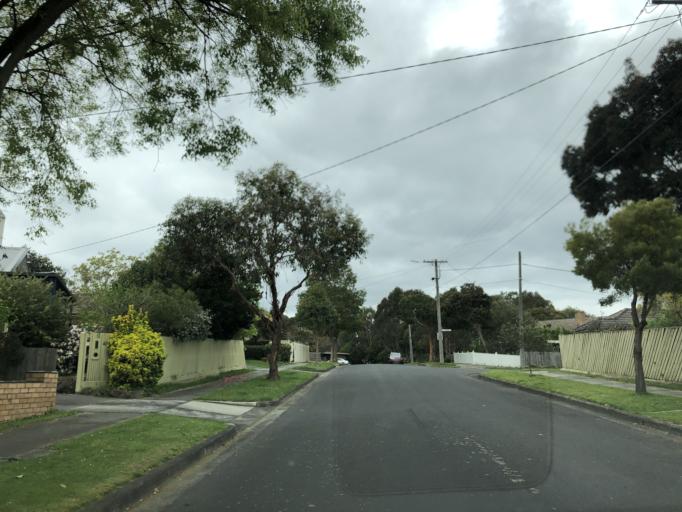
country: AU
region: Victoria
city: Burwood East
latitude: -37.8405
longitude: 145.1401
